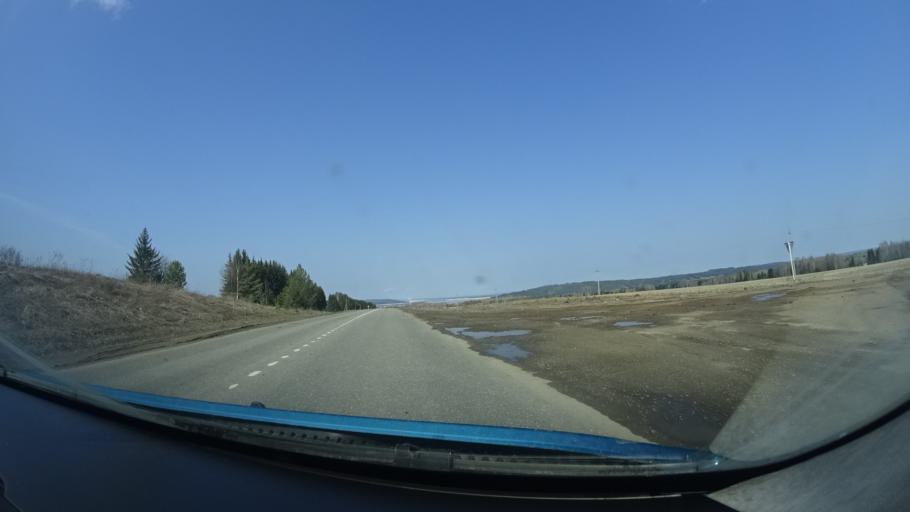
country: RU
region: Perm
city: Osa
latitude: 57.2677
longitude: 55.5726
